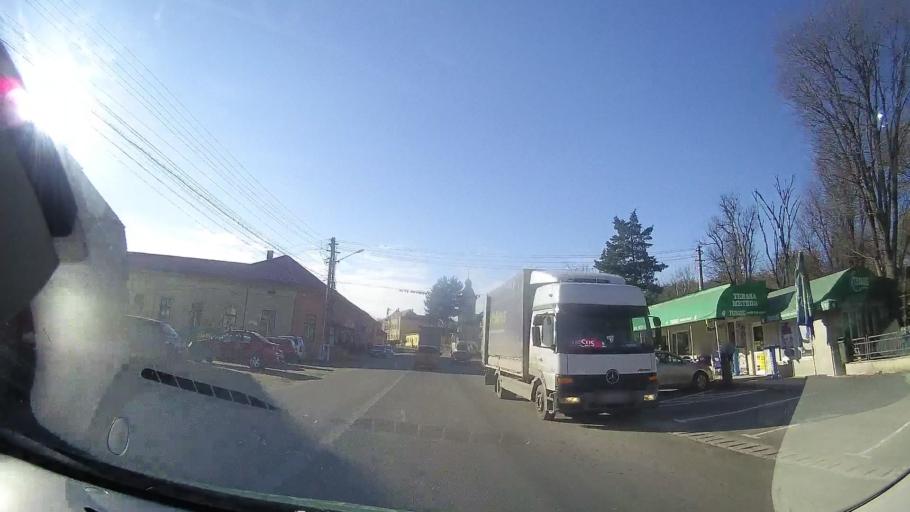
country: RO
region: Cluj
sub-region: Comuna Mociu
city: Mociu
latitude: 46.7976
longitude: 24.0328
